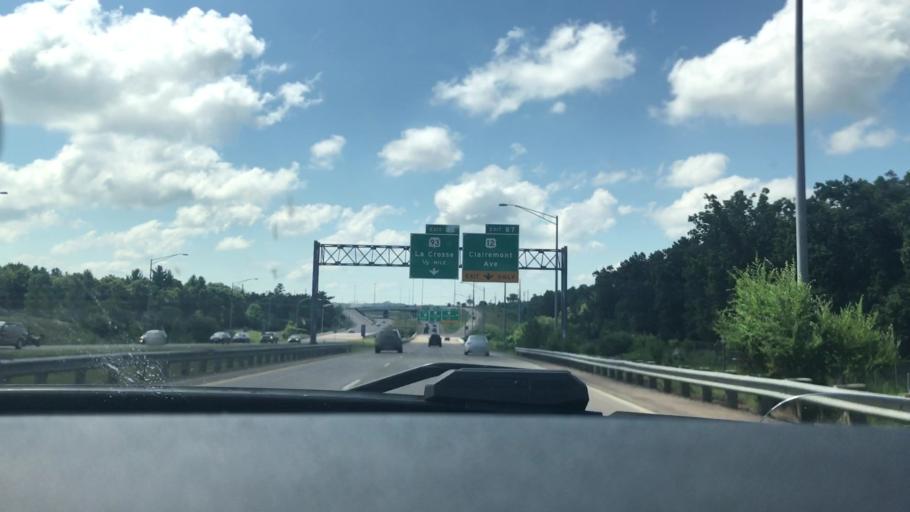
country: US
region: Wisconsin
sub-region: Eau Claire County
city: Altoona
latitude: 44.8027
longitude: -91.4559
